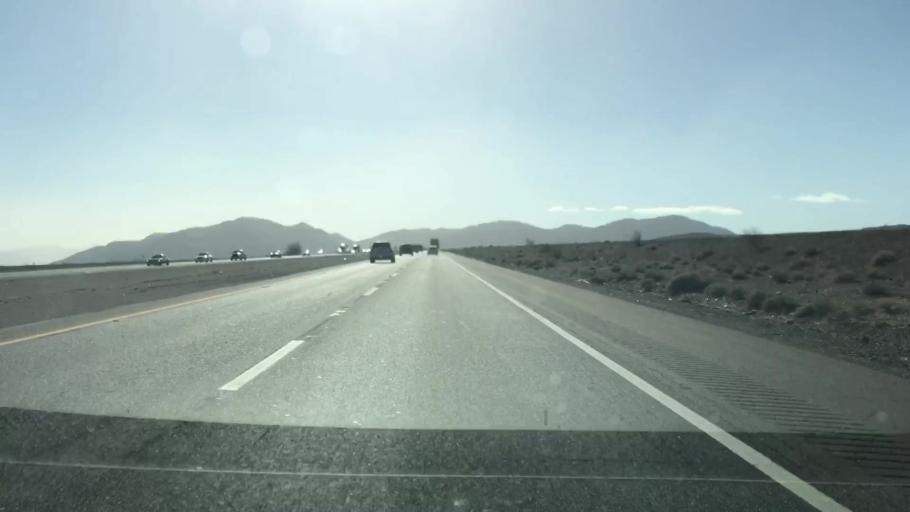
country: US
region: California
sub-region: San Bernardino County
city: Fort Irwin
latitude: 35.2311
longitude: -116.1034
